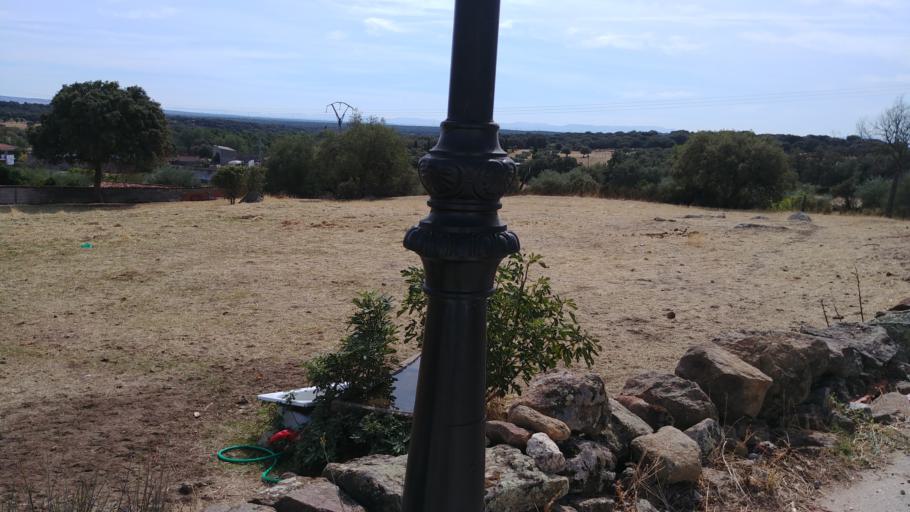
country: ES
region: Castille-La Mancha
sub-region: Province of Toledo
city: Navalcan
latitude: 40.0661
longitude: -5.0957
